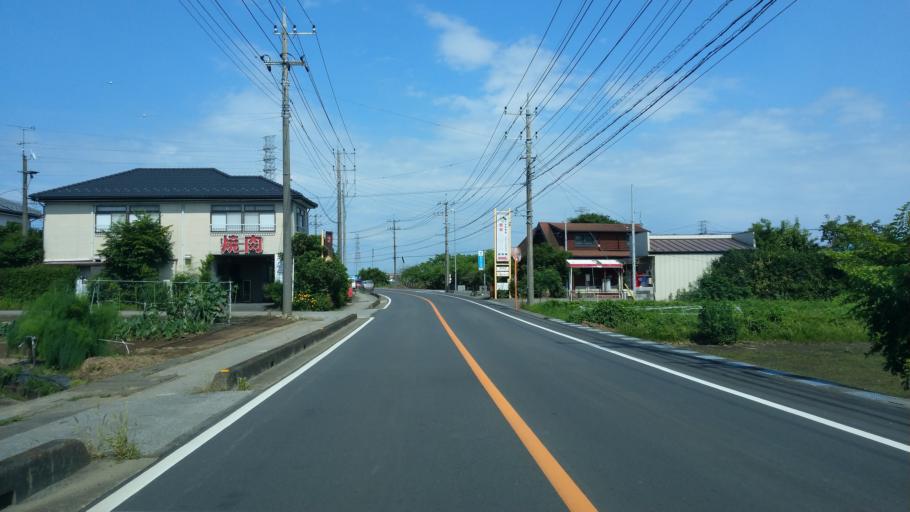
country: JP
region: Saitama
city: Kodamacho-kodamaminami
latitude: 36.2048
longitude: 139.1587
